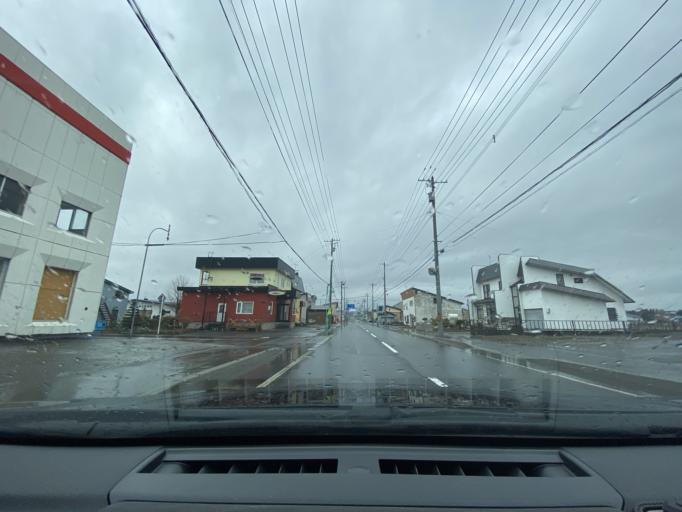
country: JP
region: Hokkaido
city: Fukagawa
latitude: 43.8085
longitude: 141.9435
